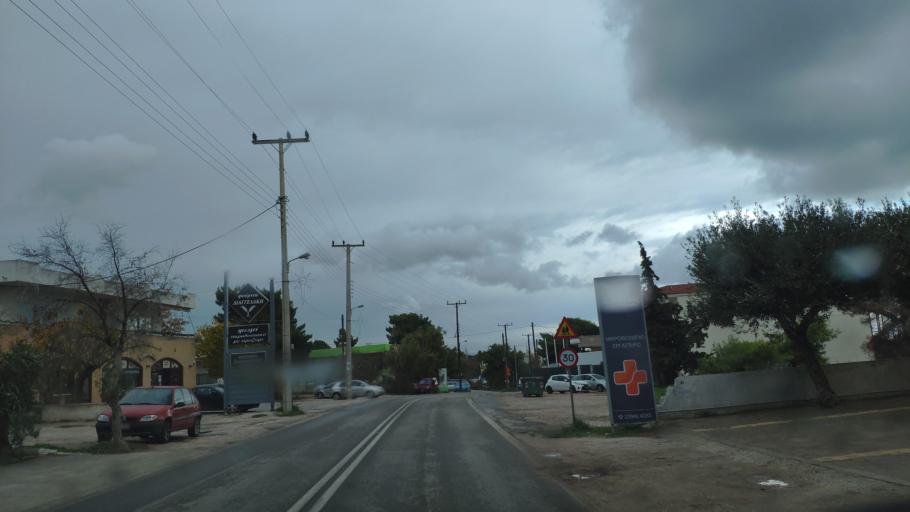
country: GR
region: Attica
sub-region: Nomarchia Anatolikis Attikis
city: Artemida
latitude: 37.9572
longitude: 24.0055
